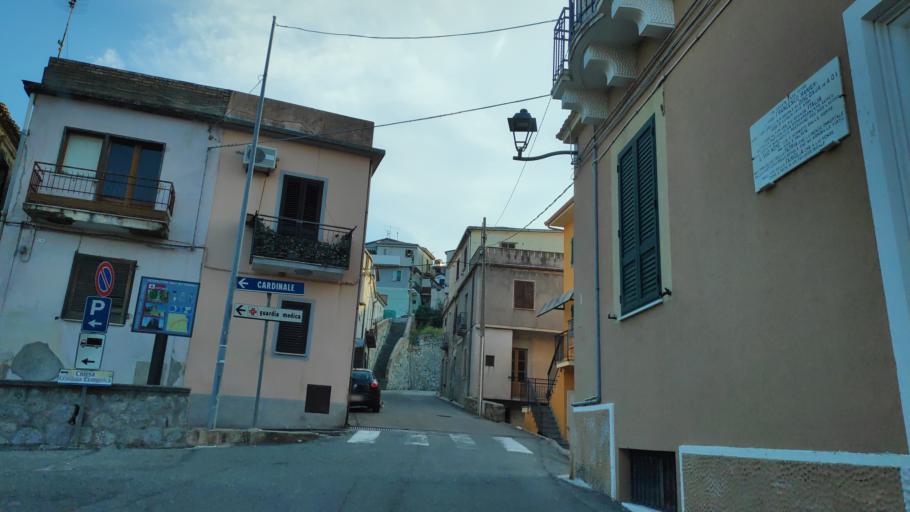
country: IT
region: Calabria
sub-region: Provincia di Catanzaro
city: Satriano
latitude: 38.6674
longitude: 16.4825
